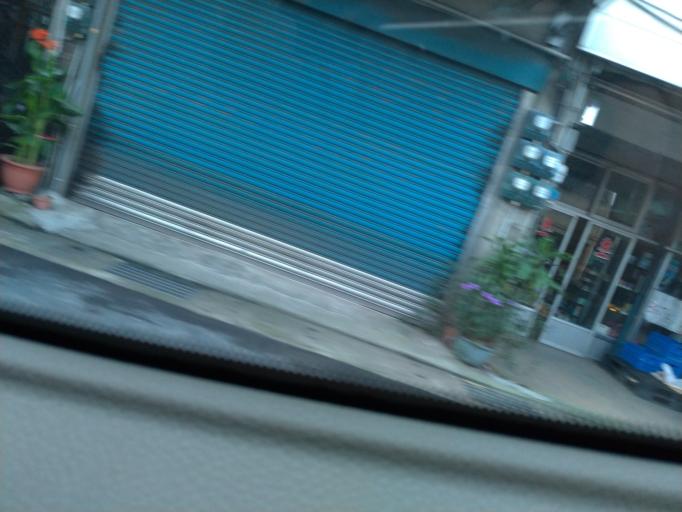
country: TW
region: Taiwan
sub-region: Taoyuan
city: Taoyuan
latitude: 24.9362
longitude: 121.3956
